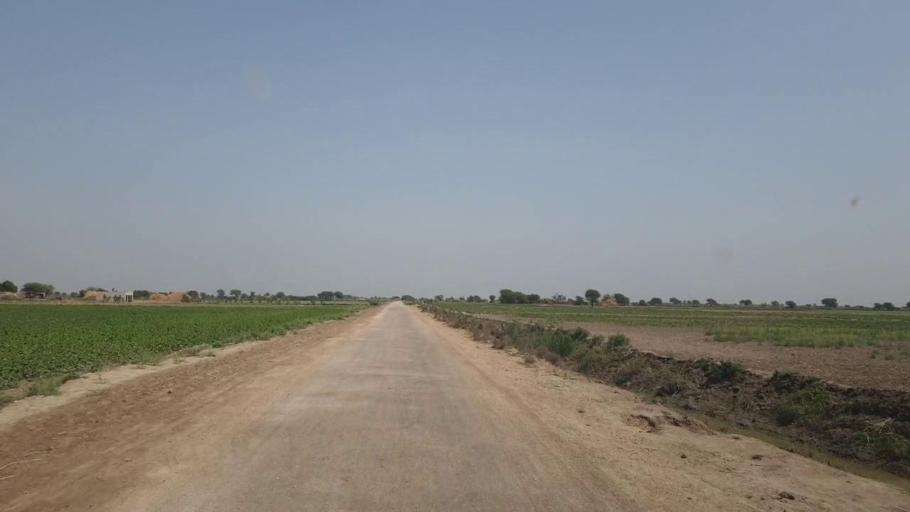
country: PK
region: Sindh
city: Jati
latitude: 24.4774
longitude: 68.5509
